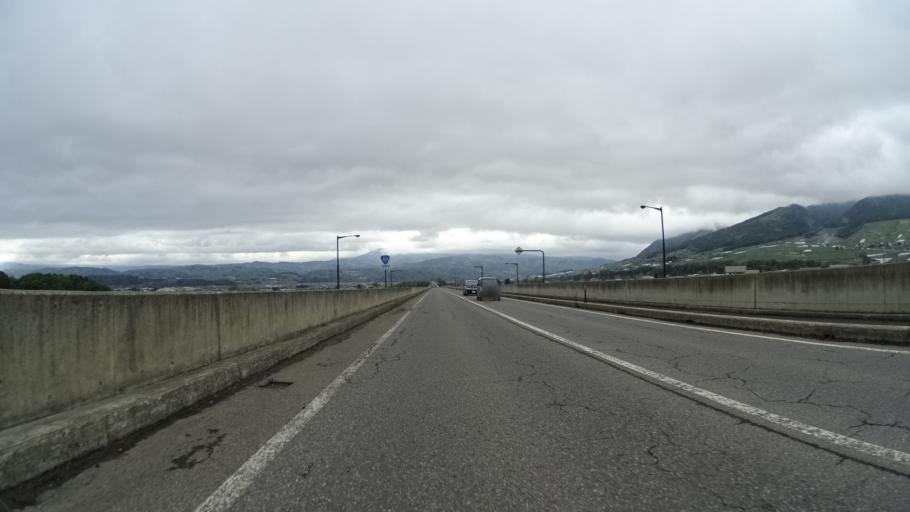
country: JP
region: Nagano
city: Nakano
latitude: 36.7566
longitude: 138.3932
